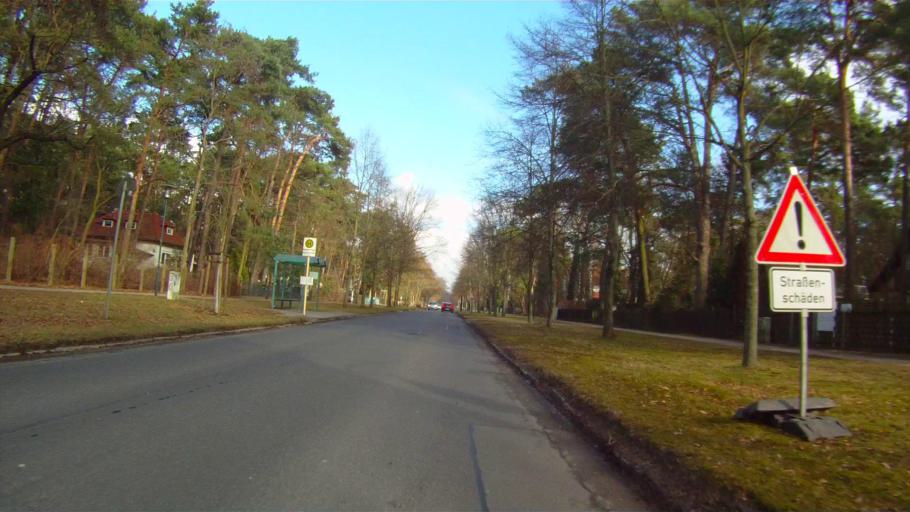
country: DE
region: Berlin
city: Friedrichshagen
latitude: 52.4803
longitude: 13.6235
